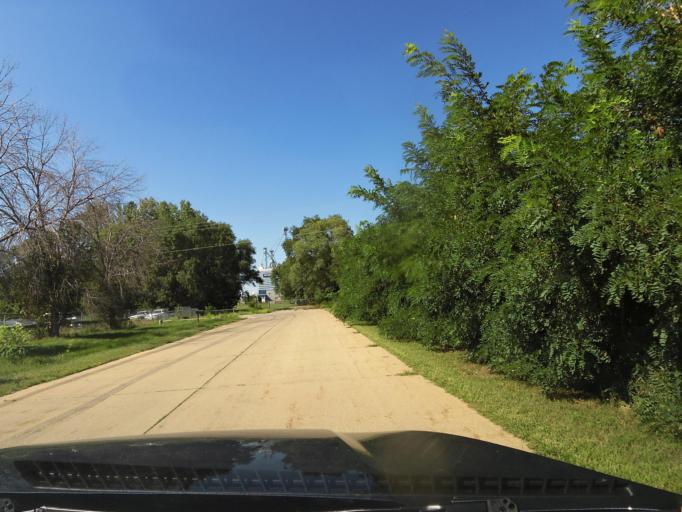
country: US
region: Iowa
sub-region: Black Hawk County
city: Waterloo
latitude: 42.4725
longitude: -92.3187
